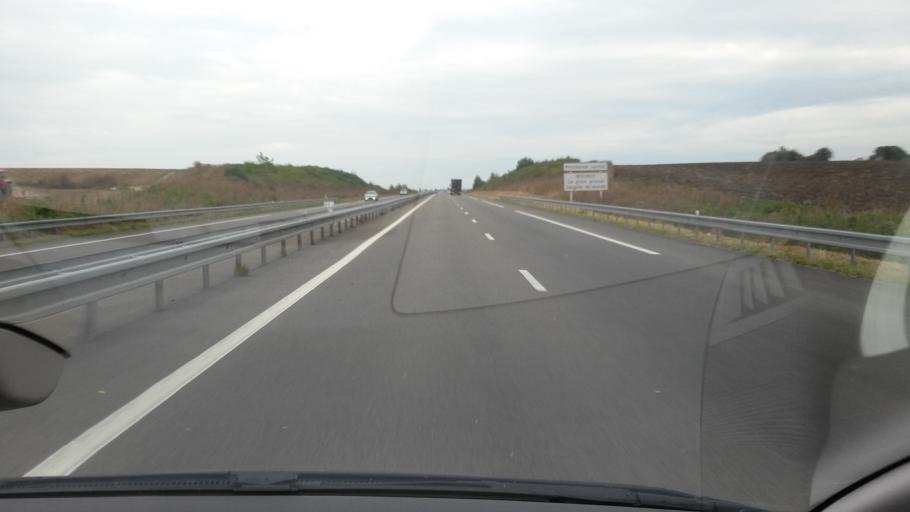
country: FR
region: Champagne-Ardenne
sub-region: Departement des Ardennes
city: Rethel
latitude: 49.5720
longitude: 4.4759
